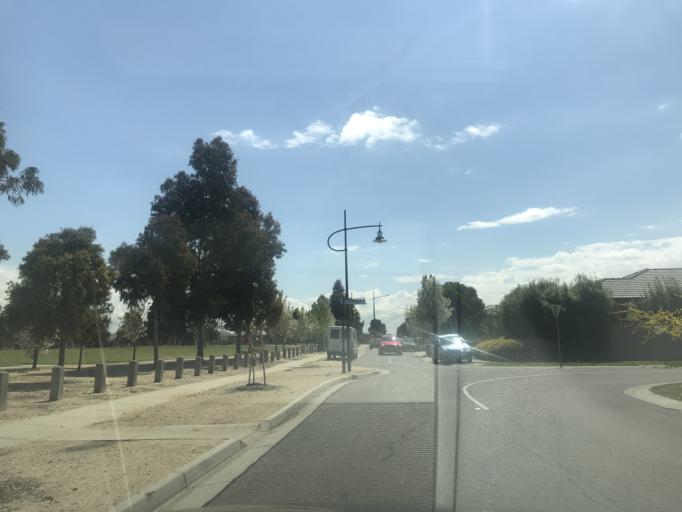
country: AU
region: Victoria
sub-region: Wyndham
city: Hoppers Crossing
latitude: -37.8871
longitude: 144.7215
